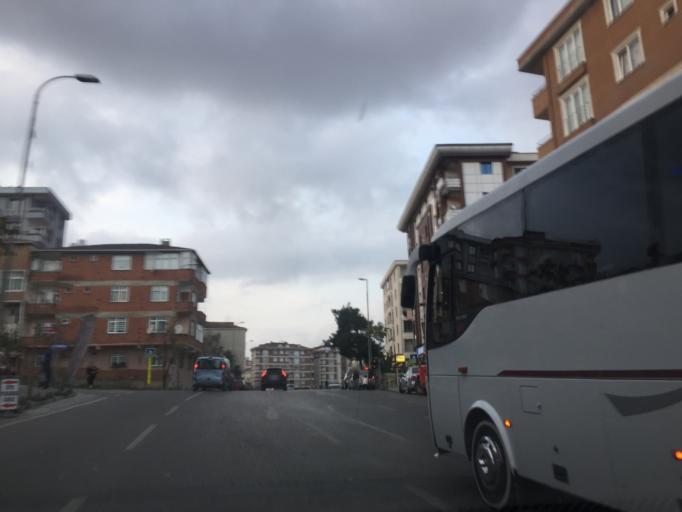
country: TR
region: Istanbul
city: Samandira
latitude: 40.9878
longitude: 29.2319
